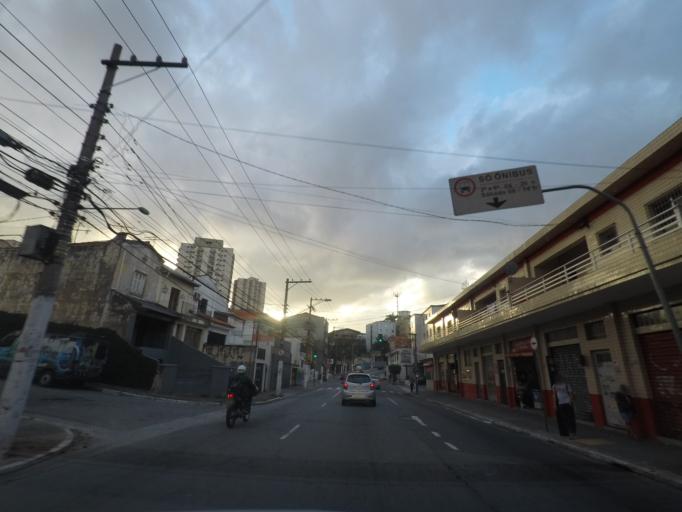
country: BR
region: Sao Paulo
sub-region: Sao Paulo
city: Sao Paulo
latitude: -23.4927
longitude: -46.6238
